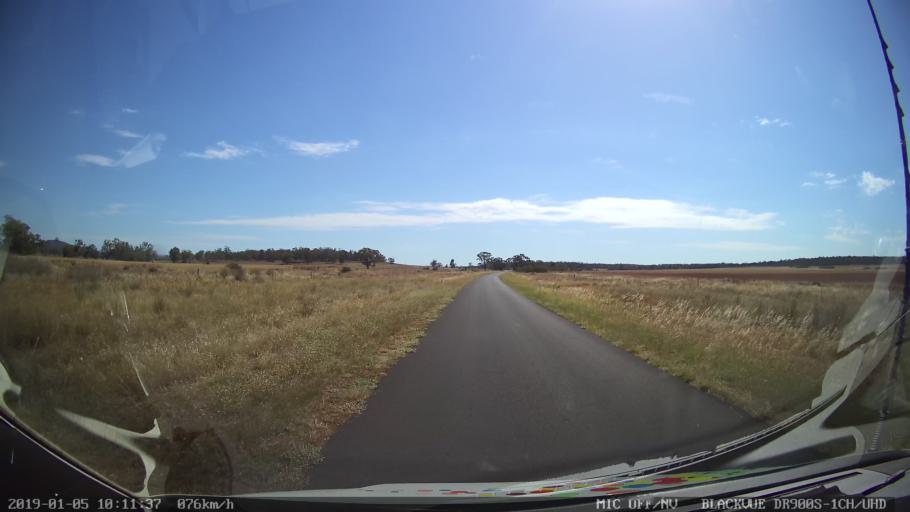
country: AU
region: New South Wales
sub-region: Gilgandra
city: Gilgandra
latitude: -31.6123
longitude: 148.9033
